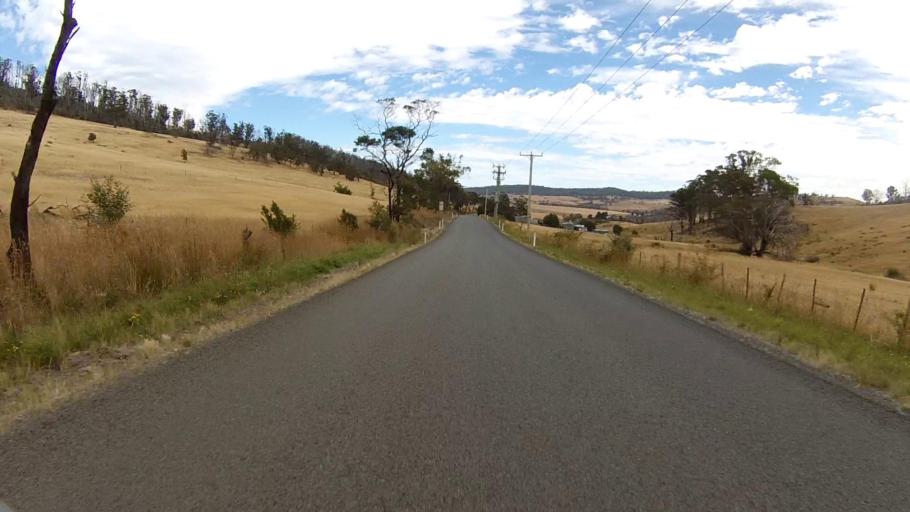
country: AU
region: Tasmania
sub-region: Sorell
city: Sorell
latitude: -42.8788
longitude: 147.7104
